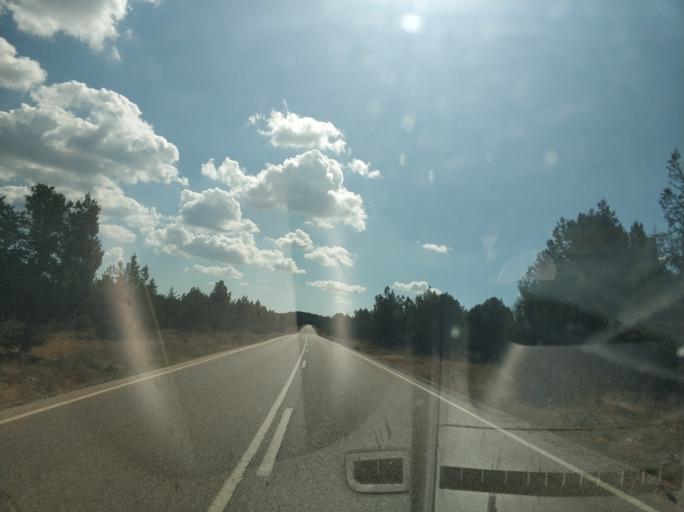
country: ES
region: Castille and Leon
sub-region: Provincia de Soria
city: Ucero
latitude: 41.7388
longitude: -3.0446
